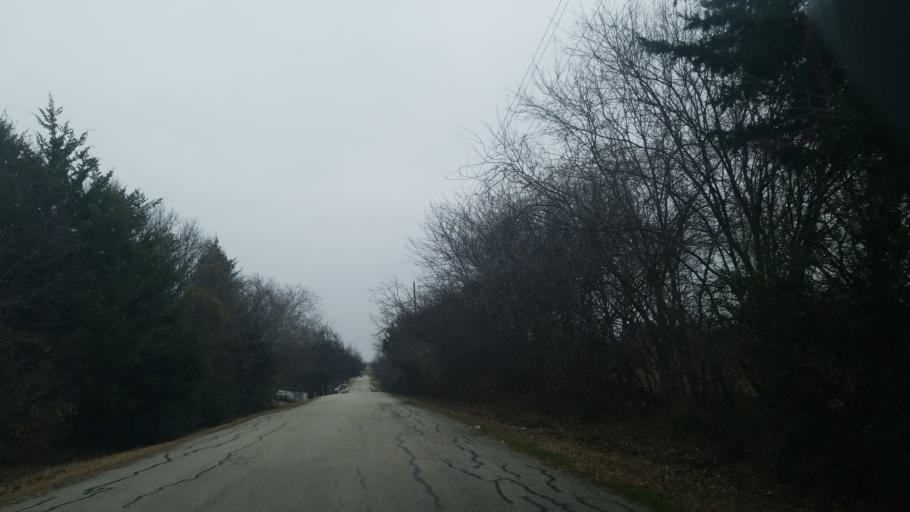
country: US
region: Texas
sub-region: Denton County
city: Argyle
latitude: 33.1472
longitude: -97.1612
